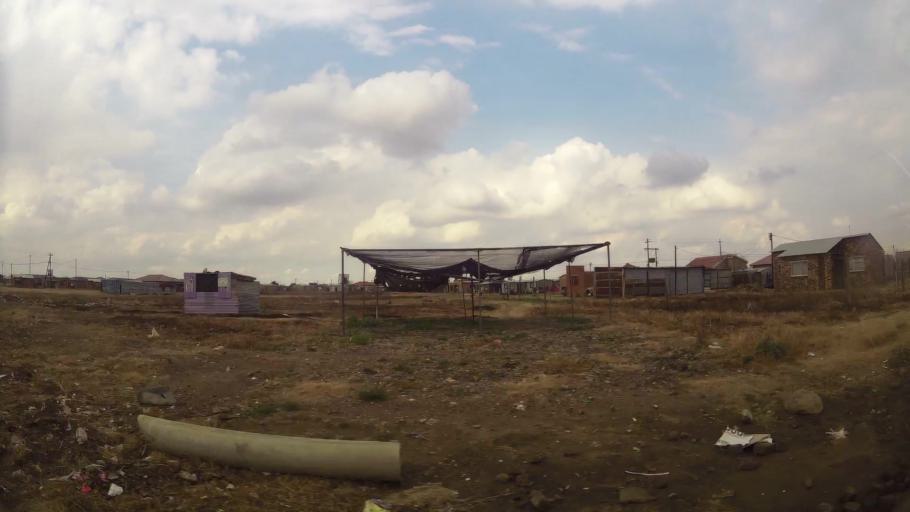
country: ZA
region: Orange Free State
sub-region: Fezile Dabi District Municipality
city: Sasolburg
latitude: -26.8592
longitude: 27.8921
